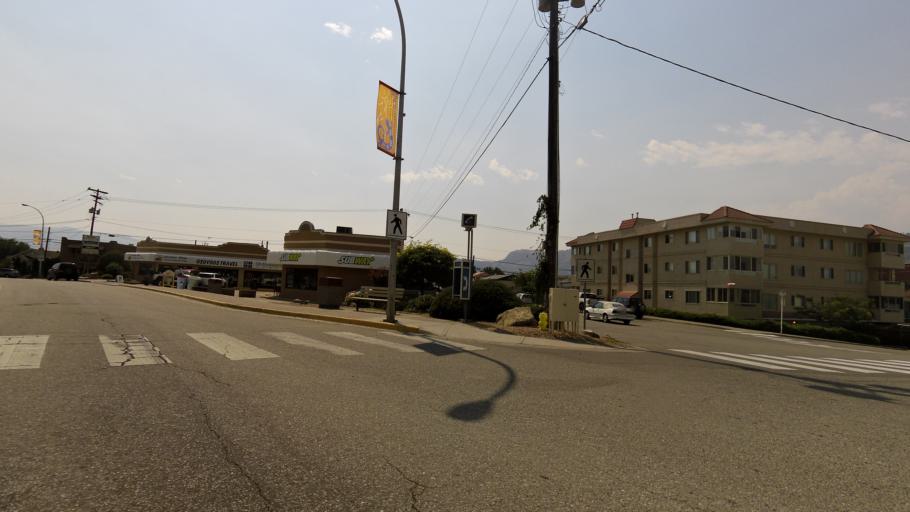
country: CA
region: British Columbia
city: Osoyoos
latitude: 49.0305
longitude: -119.4630
